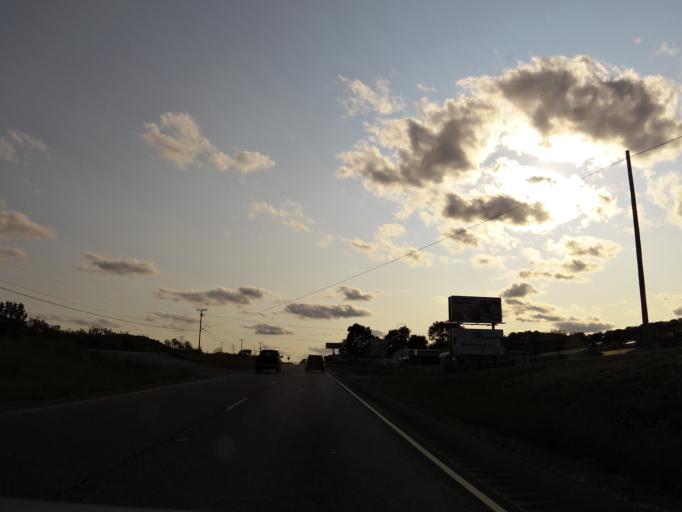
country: US
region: Virginia
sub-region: Tazewell County
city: Claypool Hill
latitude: 37.0689
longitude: -81.7283
